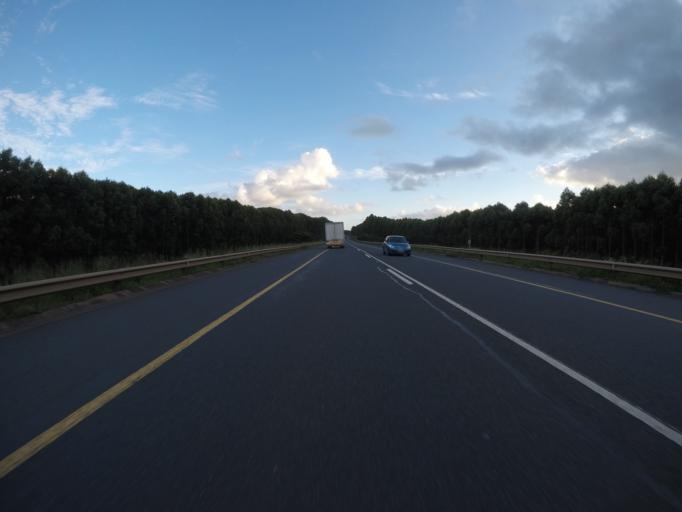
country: ZA
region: KwaZulu-Natal
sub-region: uThungulu District Municipality
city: KwaMbonambi
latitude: -28.5847
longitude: 32.0990
